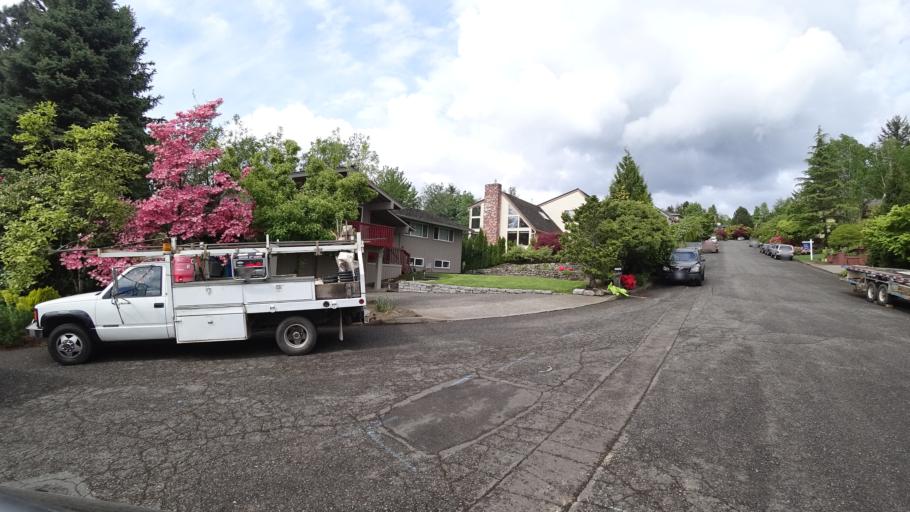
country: US
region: Oregon
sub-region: Washington County
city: West Haven
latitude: 45.5388
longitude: -122.7650
